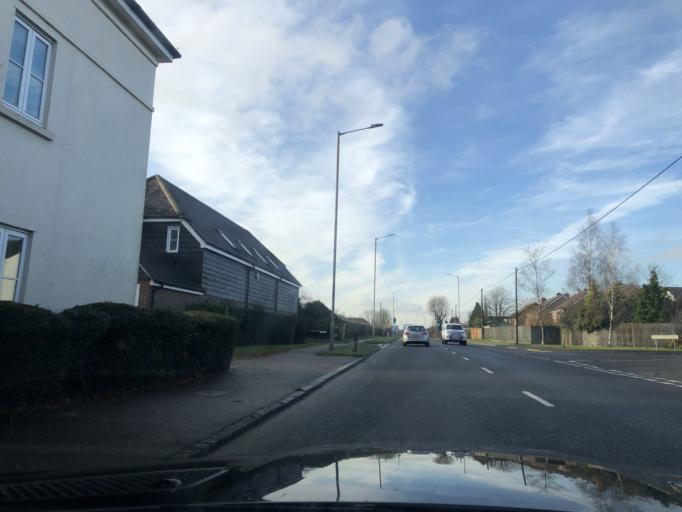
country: GB
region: England
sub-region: Buckinghamshire
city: Stokenchurch
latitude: 51.6609
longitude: -0.9057
